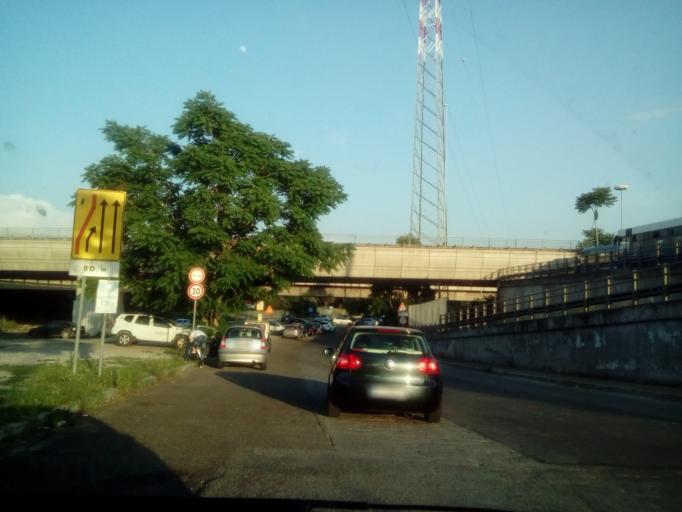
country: IT
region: Latium
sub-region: Citta metropolitana di Roma Capitale
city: Rome
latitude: 41.9230
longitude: 12.5651
